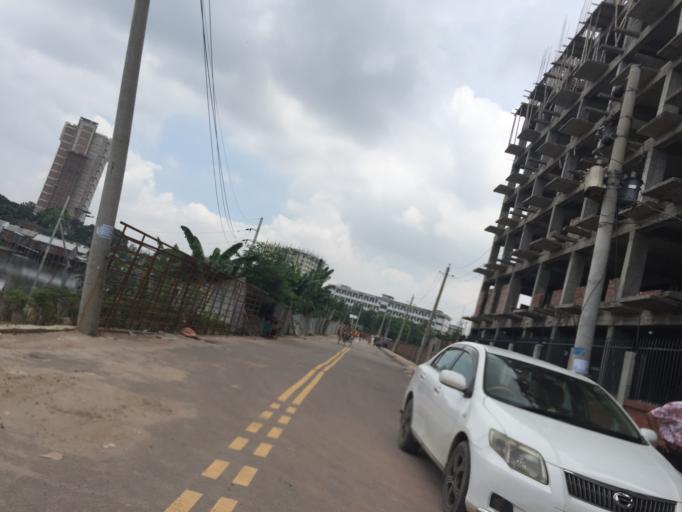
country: BD
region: Dhaka
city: Paltan
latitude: 23.8056
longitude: 90.3852
